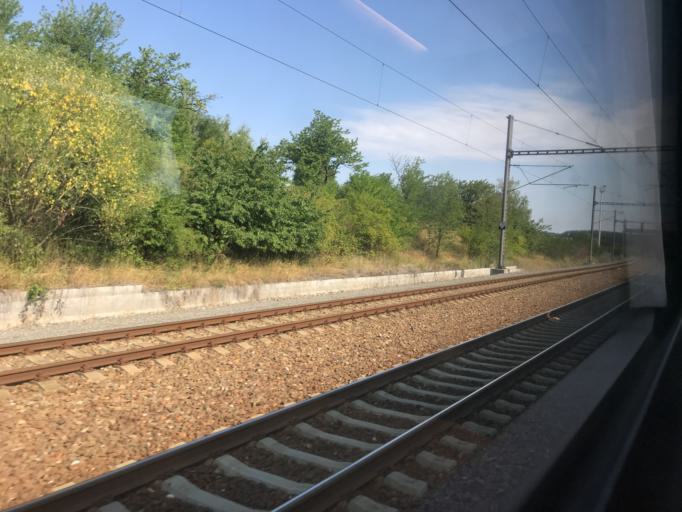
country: CZ
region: Central Bohemia
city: Votice
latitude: 49.6708
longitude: 14.6260
